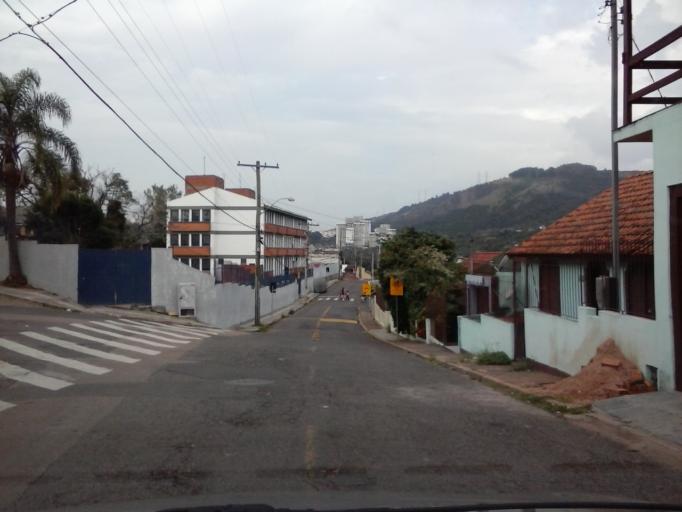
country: BR
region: Rio Grande do Sul
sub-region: Porto Alegre
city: Porto Alegre
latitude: -30.0546
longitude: -51.1510
